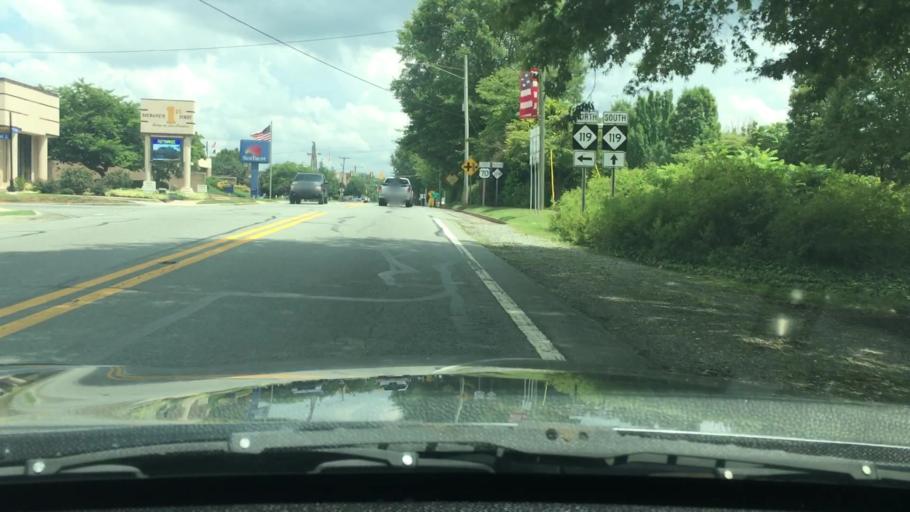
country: US
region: North Carolina
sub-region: Alamance County
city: Mebane
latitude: 36.0972
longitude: -79.2713
